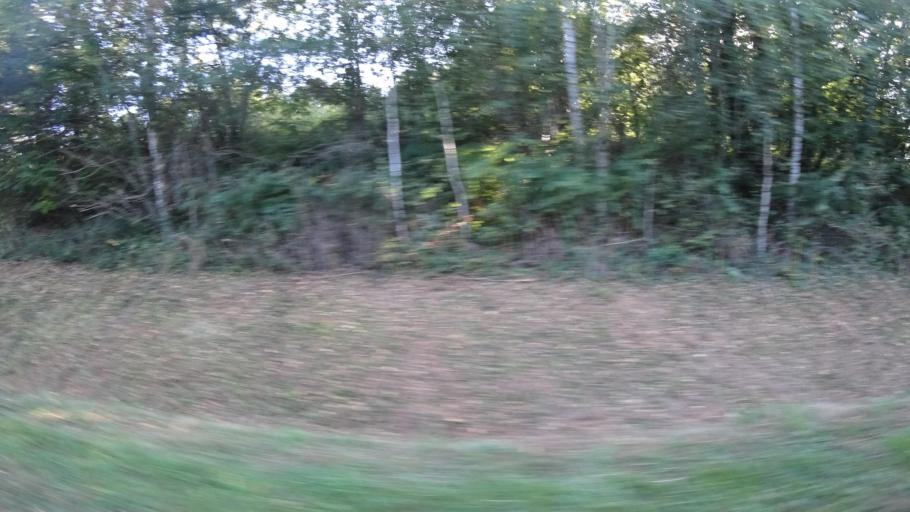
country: FR
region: Midi-Pyrenees
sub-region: Departement de l'Aveyron
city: Firmi
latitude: 44.5209
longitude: 2.3059
